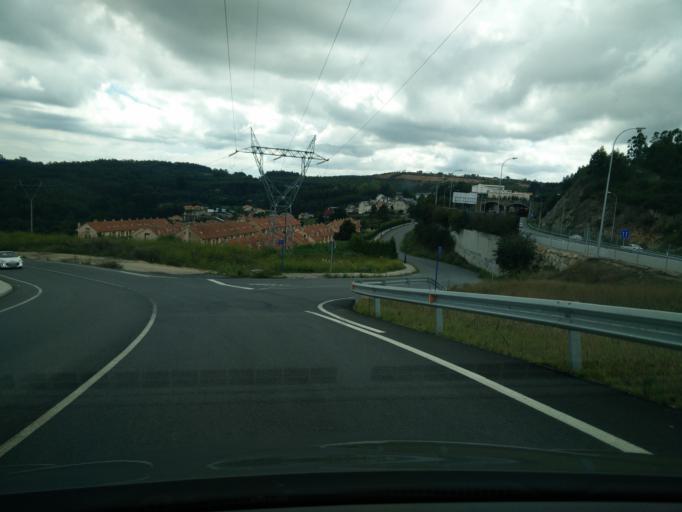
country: ES
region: Galicia
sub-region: Provincia da Coruna
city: Culleredo
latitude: 43.3222
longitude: -8.4085
